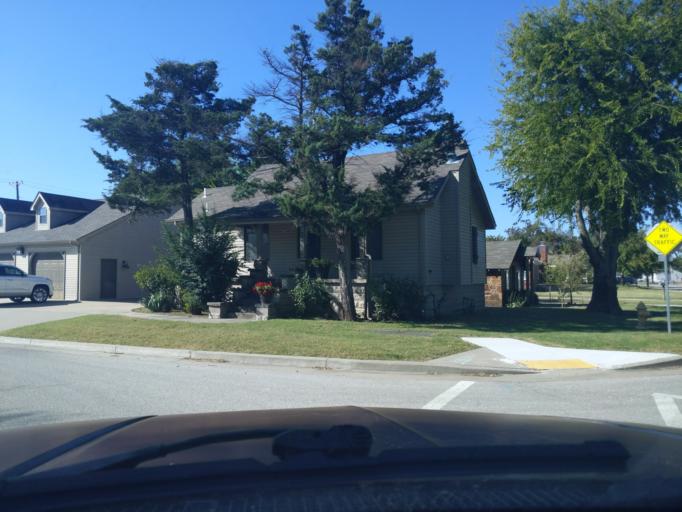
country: US
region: Oklahoma
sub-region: Tulsa County
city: Jenks
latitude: 36.0236
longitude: -95.9733
